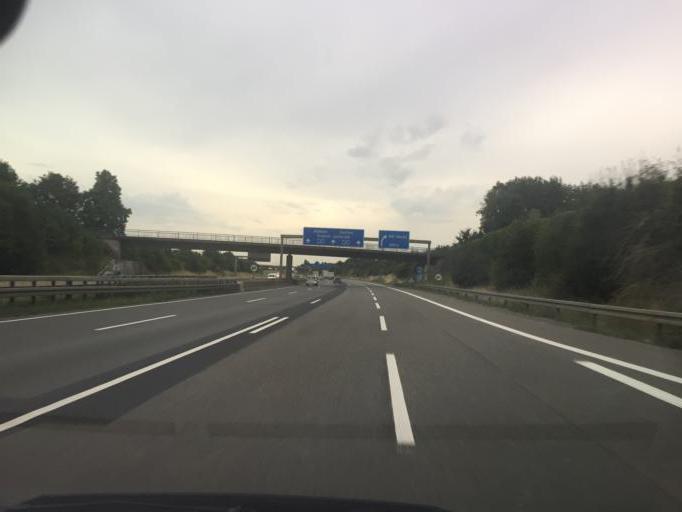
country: DE
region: North Rhine-Westphalia
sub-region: Regierungsbezirk Dusseldorf
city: Juchen
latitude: 51.0982
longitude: 6.4223
